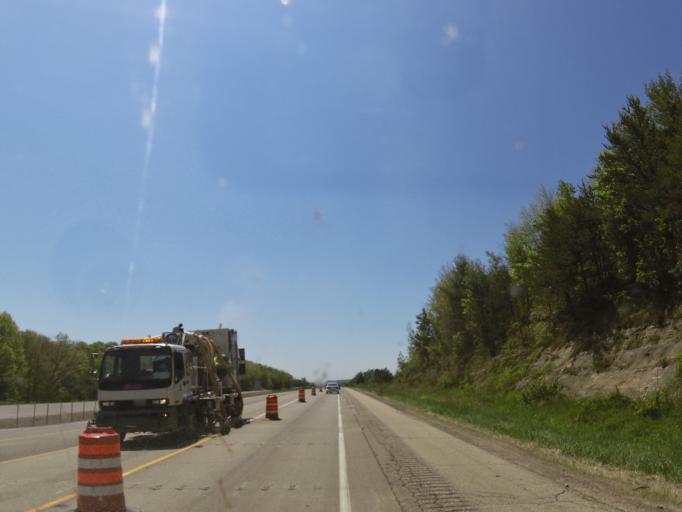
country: US
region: Wisconsin
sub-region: Monroe County
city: Tomah
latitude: 44.1117
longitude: -90.5336
